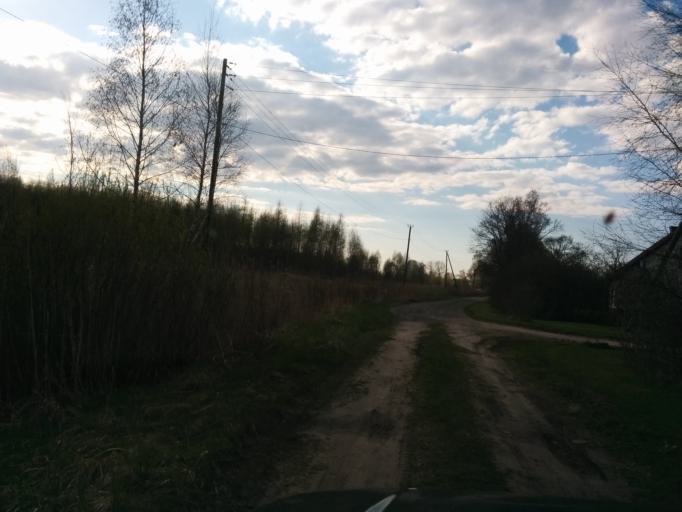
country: LV
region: Jelgava
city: Jelgava
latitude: 56.6759
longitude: 23.6699
